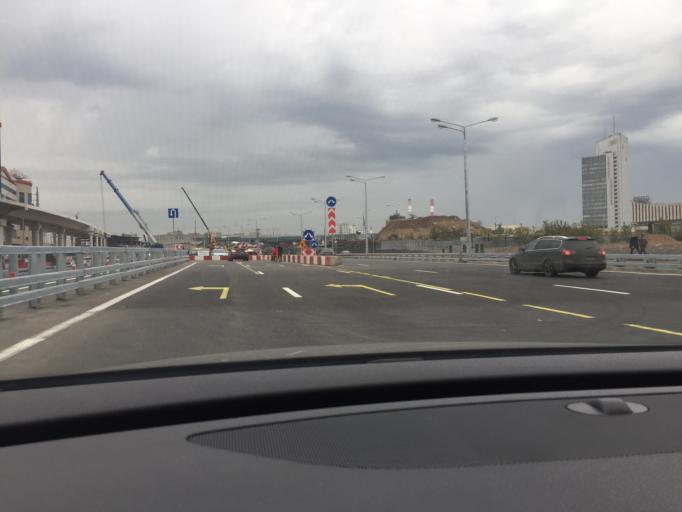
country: RU
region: Moskovskaya
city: Bogorodskoye
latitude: 55.7982
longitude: 37.7485
